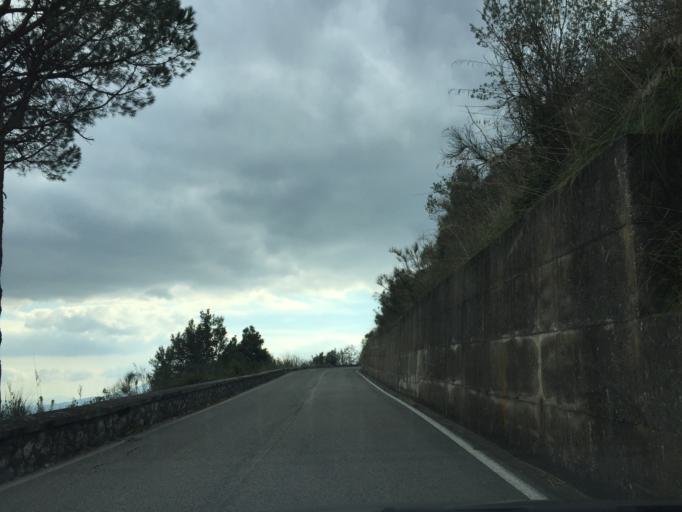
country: IT
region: Latium
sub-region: Provincia di Frosinone
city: Cassino
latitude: 41.4889
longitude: 13.8193
